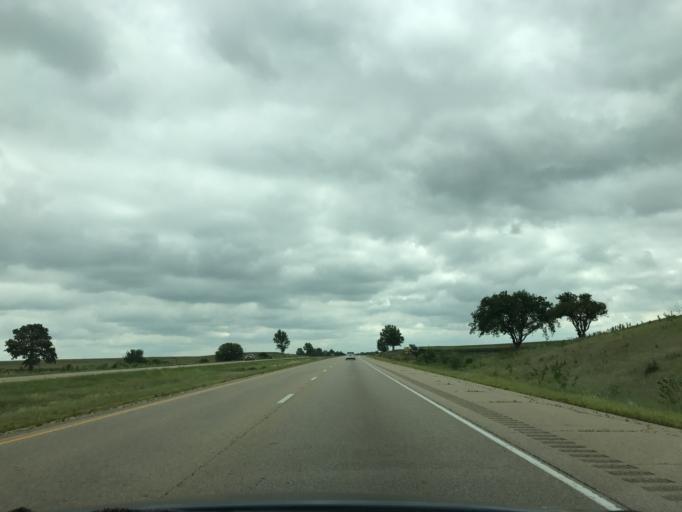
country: US
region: Illinois
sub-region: Bureau County
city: Ladd
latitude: 41.3844
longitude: -89.2718
